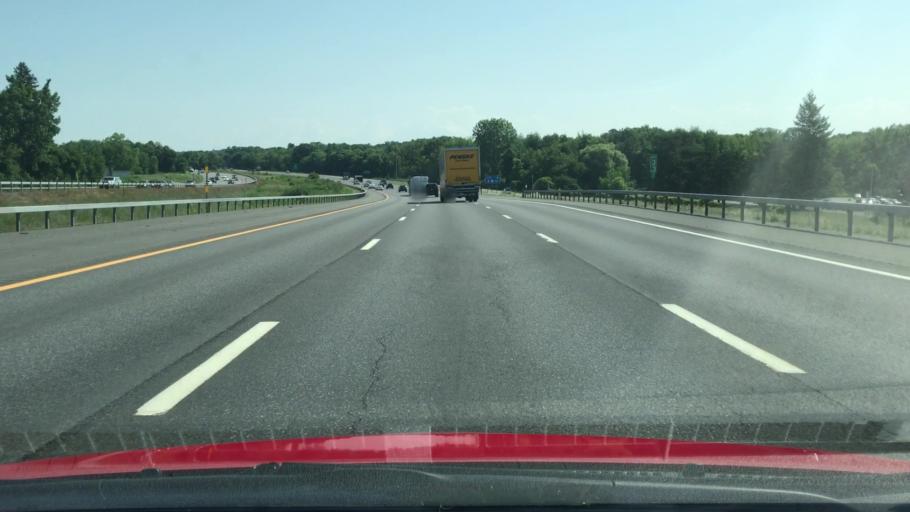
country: US
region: New York
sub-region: Albany County
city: Roessleville
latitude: 42.7282
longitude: -73.7953
